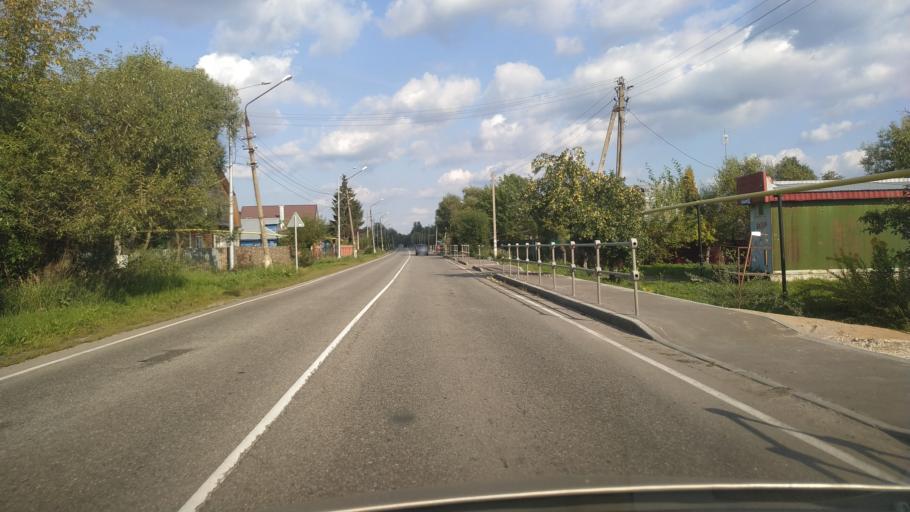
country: RU
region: Moskovskaya
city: Likino-Dulevo
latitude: 55.7298
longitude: 39.0005
